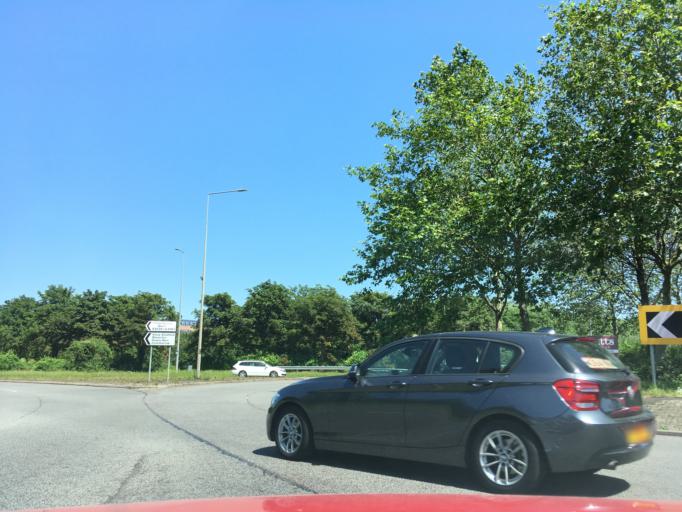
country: GB
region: England
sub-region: Milton Keynes
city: Milton Keynes
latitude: 52.0416
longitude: -0.7450
